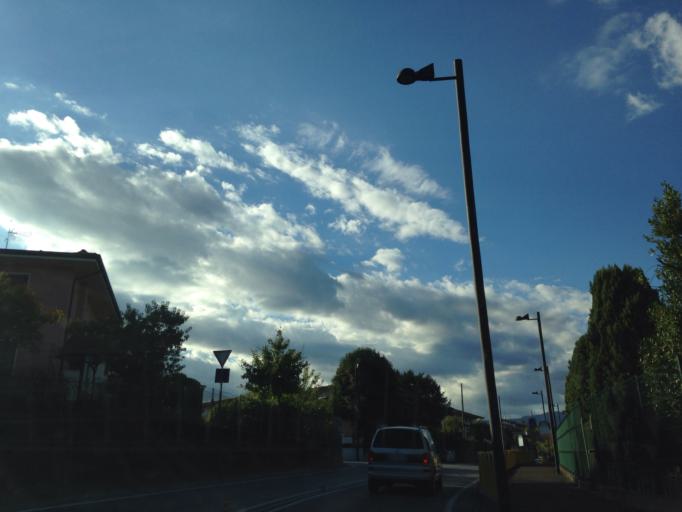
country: IT
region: Friuli Venezia Giulia
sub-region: Provincia di Pordenone
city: Porcia
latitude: 45.9580
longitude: 12.6362
